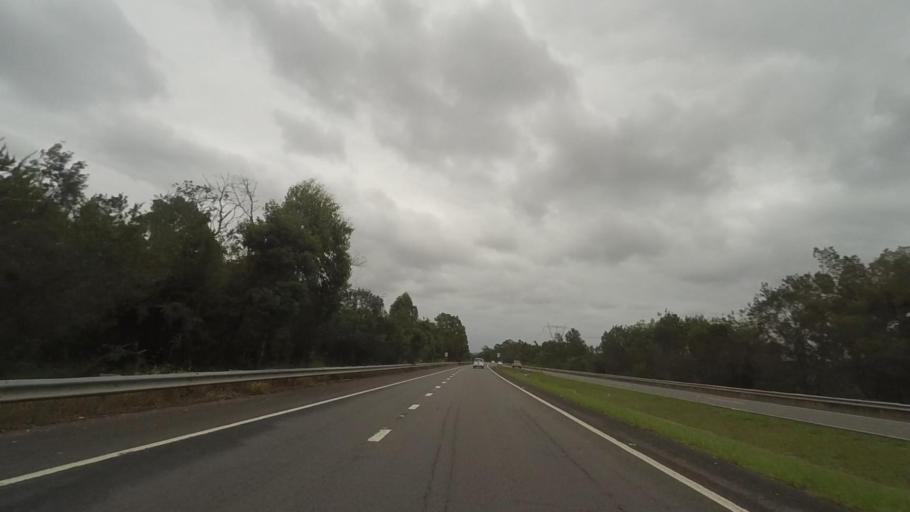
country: AU
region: New South Wales
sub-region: Wyong Shire
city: Charmhaven
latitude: -33.2054
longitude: 151.5084
